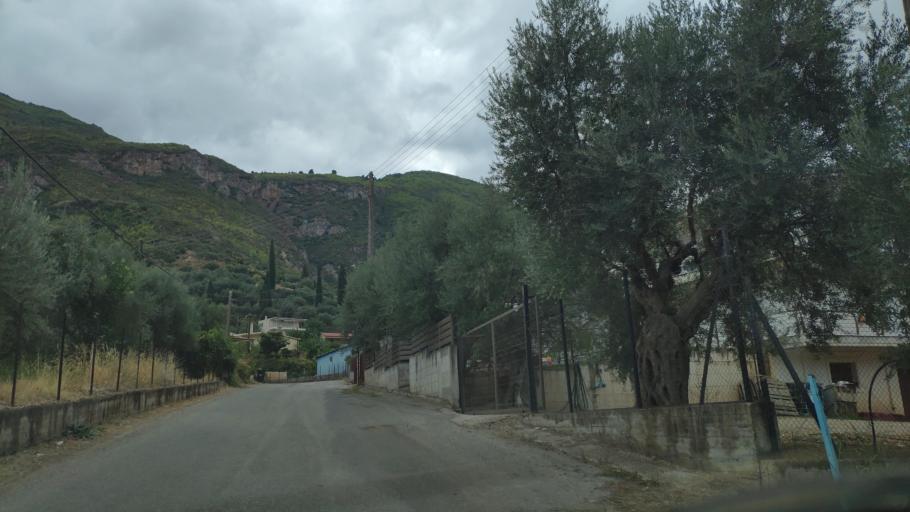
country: GR
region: West Greece
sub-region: Nomos Achaias
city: Temeni
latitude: 38.1796
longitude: 22.1444
